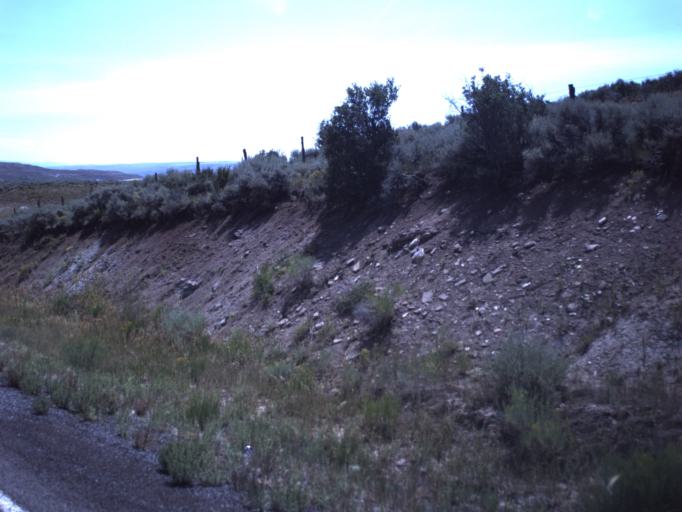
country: US
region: Utah
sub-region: Carbon County
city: Helper
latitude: 39.8607
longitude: -111.0395
